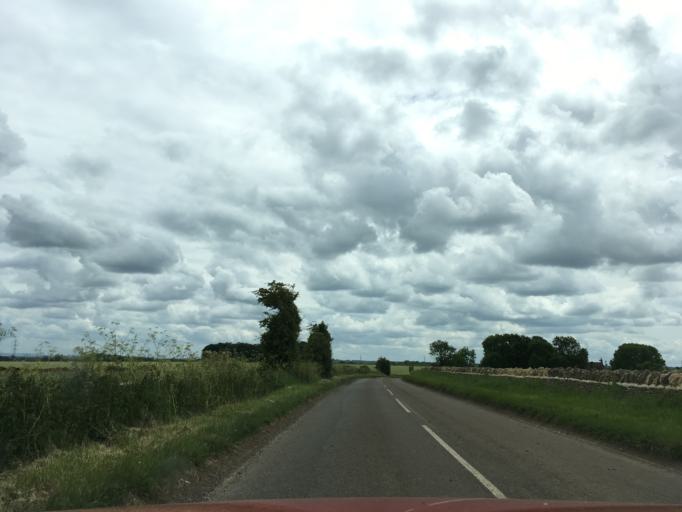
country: GB
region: England
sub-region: South Gloucestershire
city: Horton
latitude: 51.5222
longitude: -2.3352
